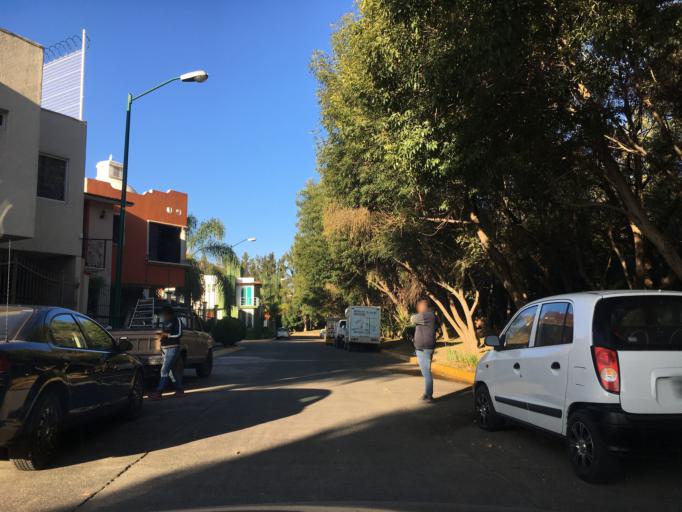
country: MX
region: Michoacan
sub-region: Morelia
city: Morelos
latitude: 19.6700
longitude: -101.2328
